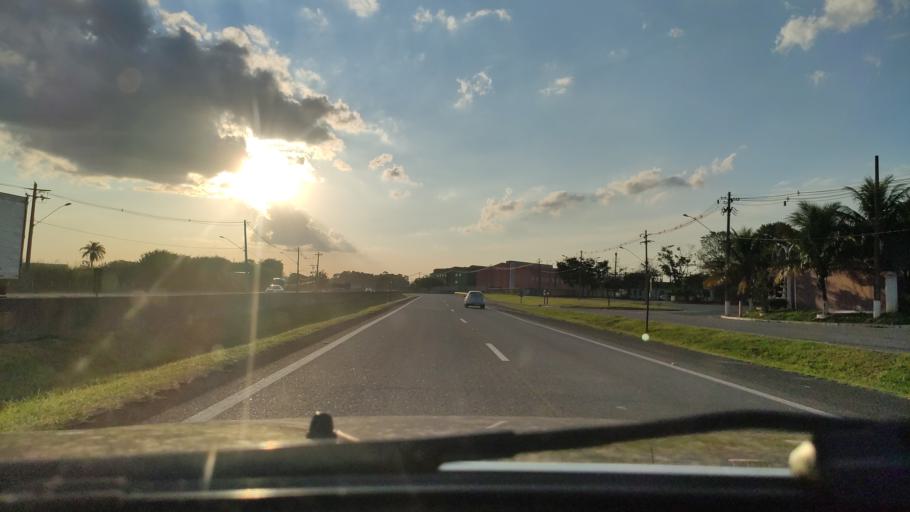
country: BR
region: Sao Paulo
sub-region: Limeira
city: Limeira
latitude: -22.5440
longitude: -47.3682
